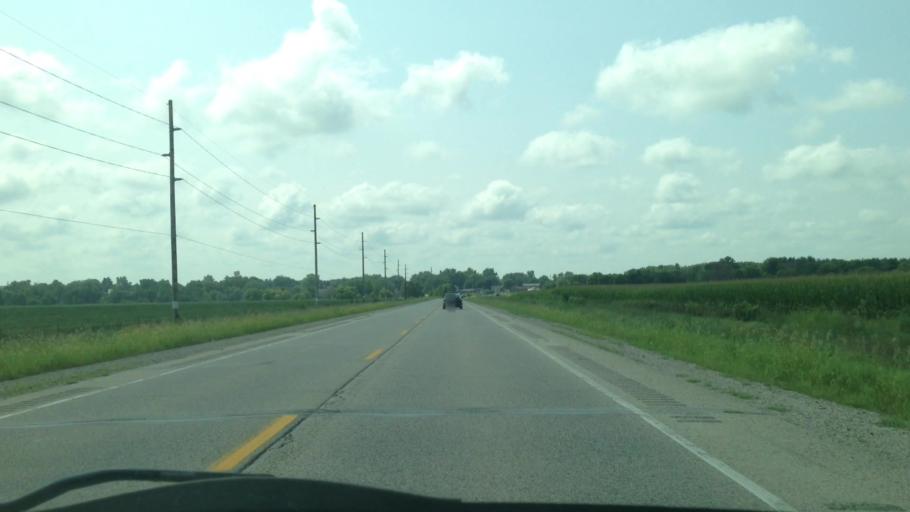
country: US
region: Iowa
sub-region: Benton County
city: Walford
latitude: 41.8105
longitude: -91.8724
